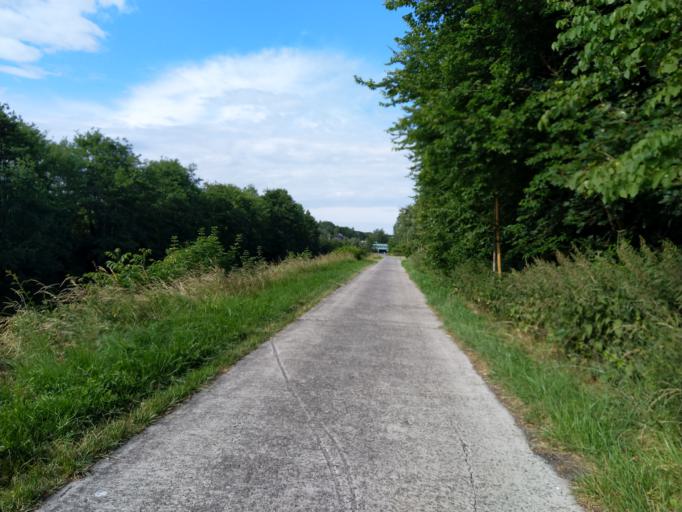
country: BE
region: Wallonia
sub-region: Province du Hainaut
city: Erquelinnes
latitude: 50.3036
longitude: 4.1159
